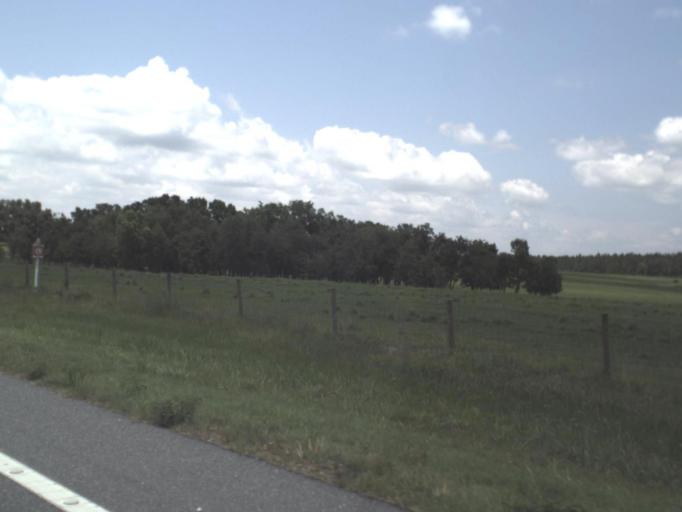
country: US
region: Florida
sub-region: Levy County
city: Williston
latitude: 29.4568
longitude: -82.4113
